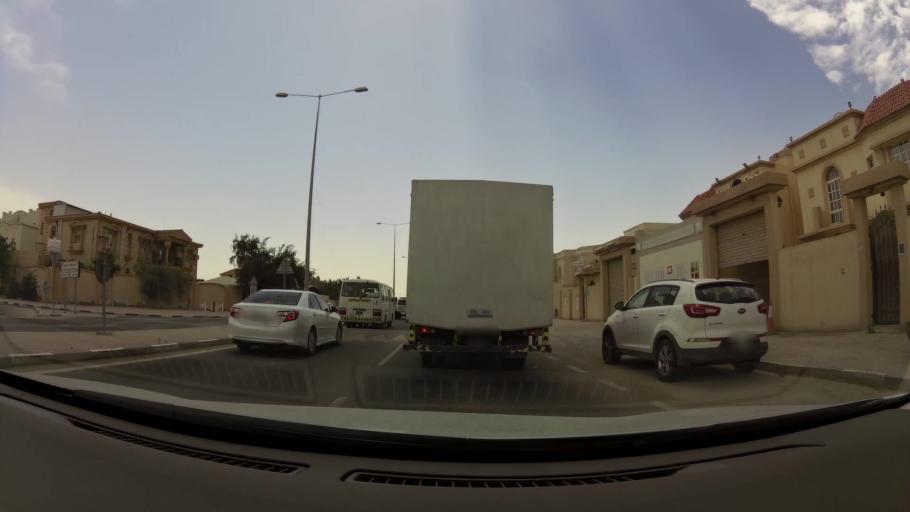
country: QA
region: Baladiyat ar Rayyan
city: Ar Rayyan
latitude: 25.2577
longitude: 51.4184
